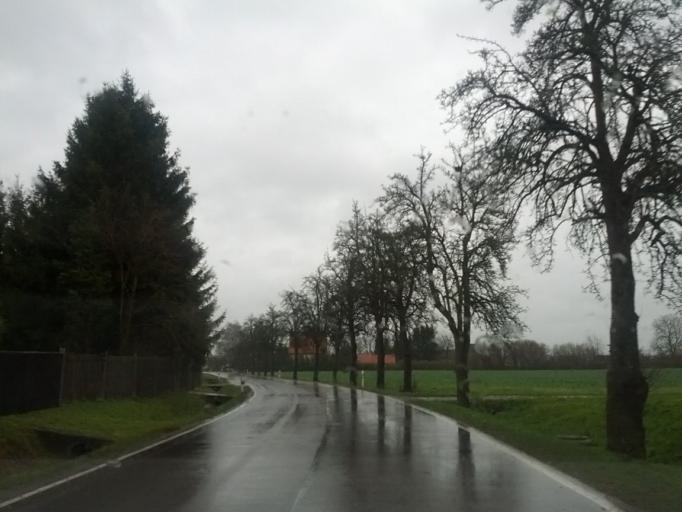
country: DE
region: Thuringia
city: Oberdorla
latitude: 51.1679
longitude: 10.4322
